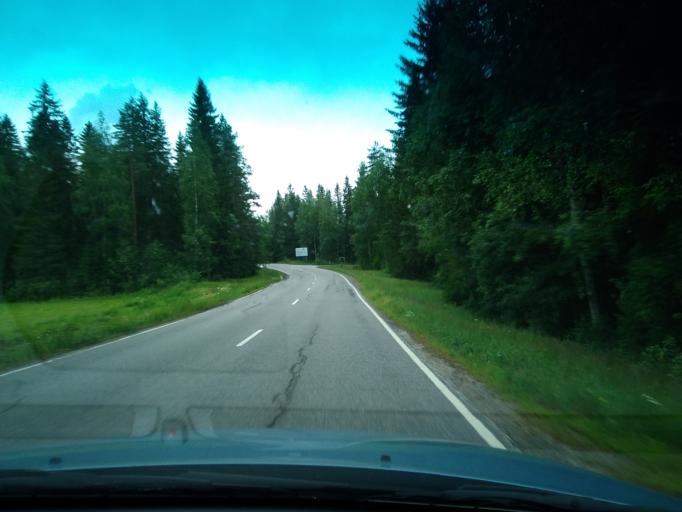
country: FI
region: Central Finland
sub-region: Keuruu
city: Multia
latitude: 62.4170
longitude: 24.7829
